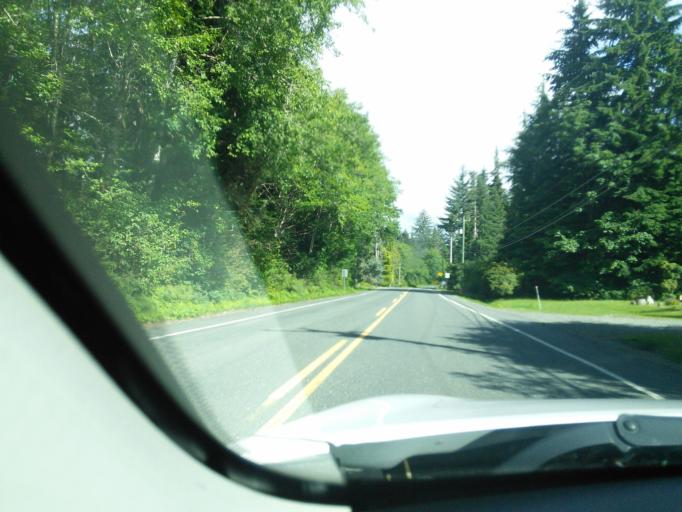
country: CA
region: British Columbia
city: Campbell River
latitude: 50.3165
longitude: -125.9214
